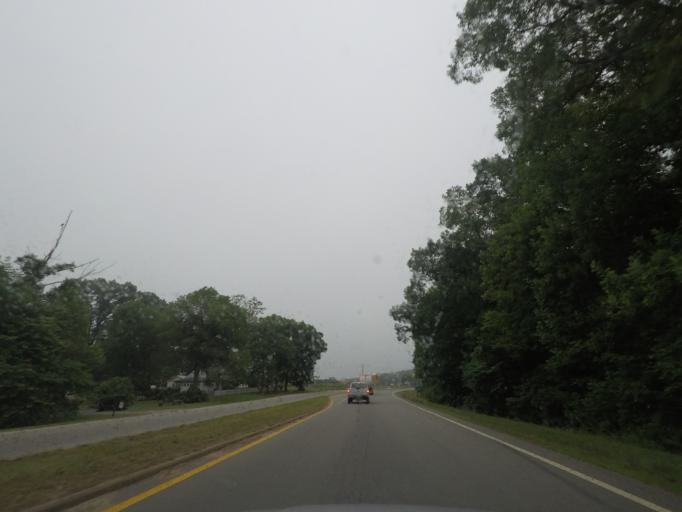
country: US
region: Virginia
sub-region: Buckingham County
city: Buckingham
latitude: 37.5268
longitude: -78.4924
